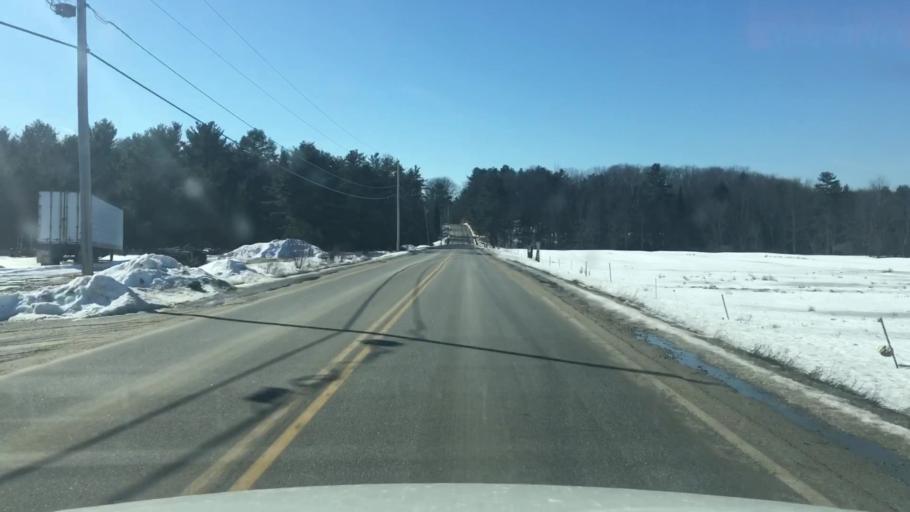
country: US
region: Maine
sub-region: Cumberland County
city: Cumberland Center
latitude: 43.8678
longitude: -70.3359
